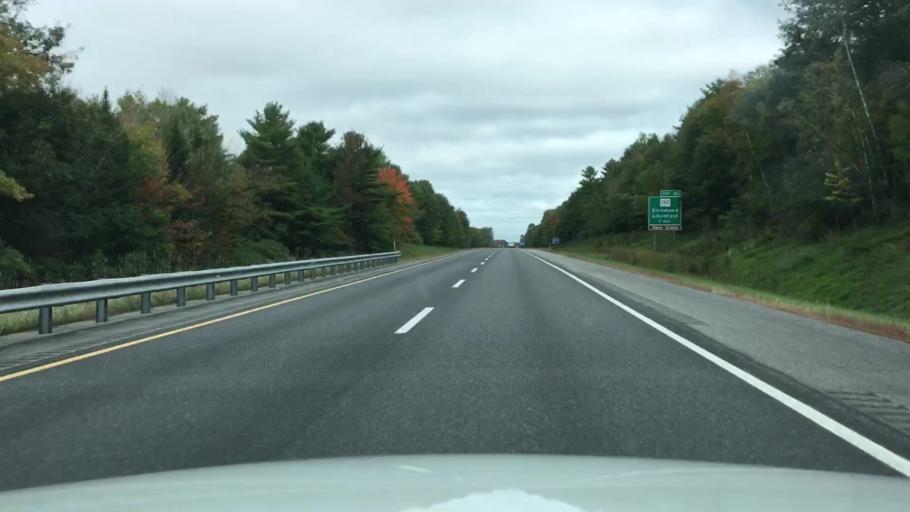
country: US
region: Maine
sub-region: Sagadahoc County
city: Richmond
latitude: 44.0794
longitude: -69.8771
